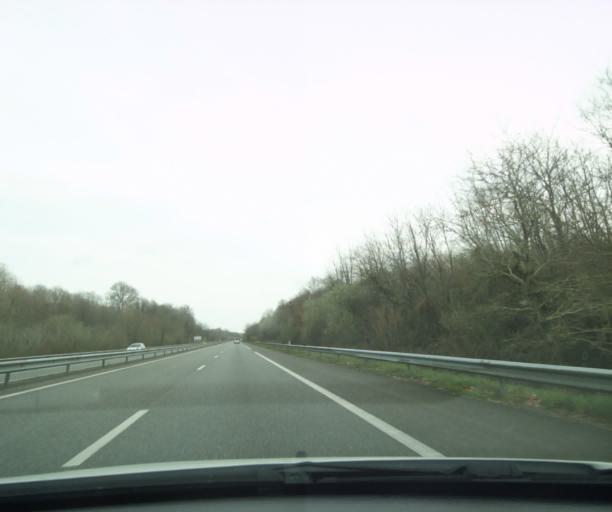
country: FR
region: Aquitaine
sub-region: Departement des Landes
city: Peyrehorade
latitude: 43.5263
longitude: -1.1458
